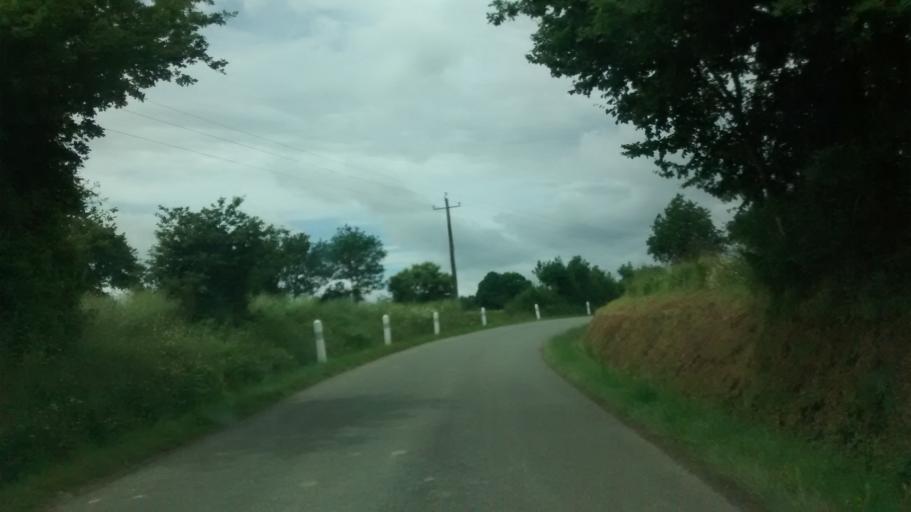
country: FR
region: Brittany
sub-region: Departement du Morbihan
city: Carentoir
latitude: 47.8027
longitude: -2.1149
